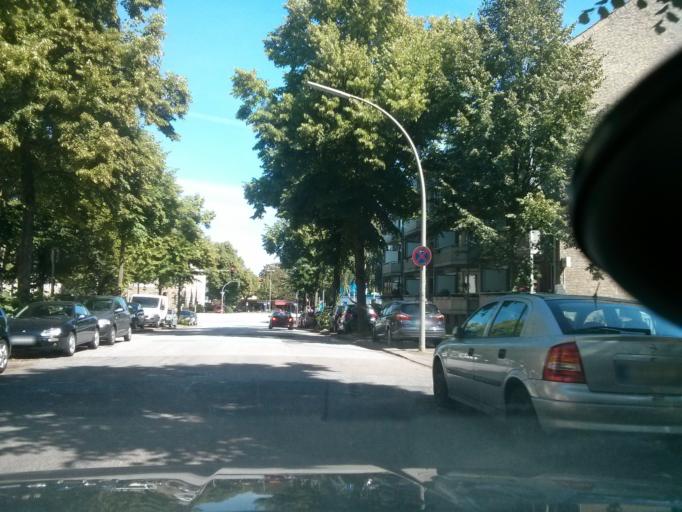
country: DE
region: Hamburg
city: Borgfelde
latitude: 53.5603
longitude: 10.0475
